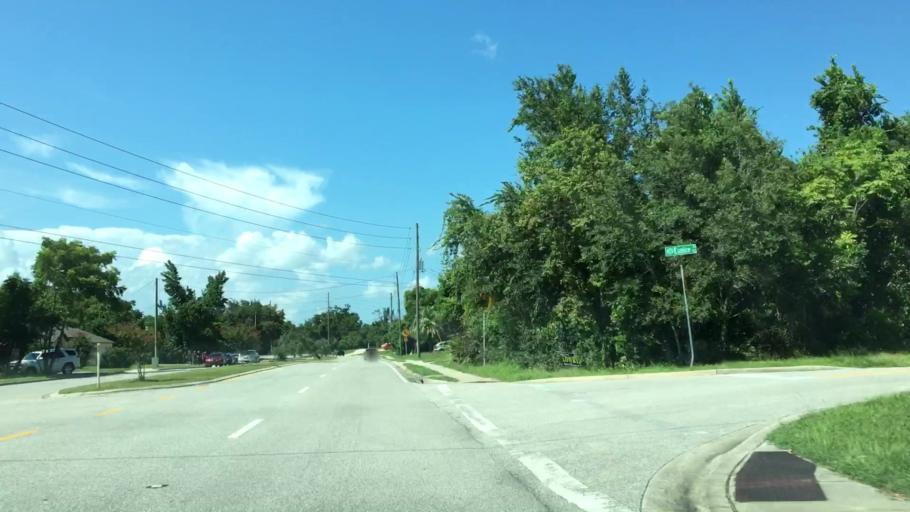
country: US
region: Florida
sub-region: Volusia County
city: Deltona
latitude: 28.9221
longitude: -81.2573
